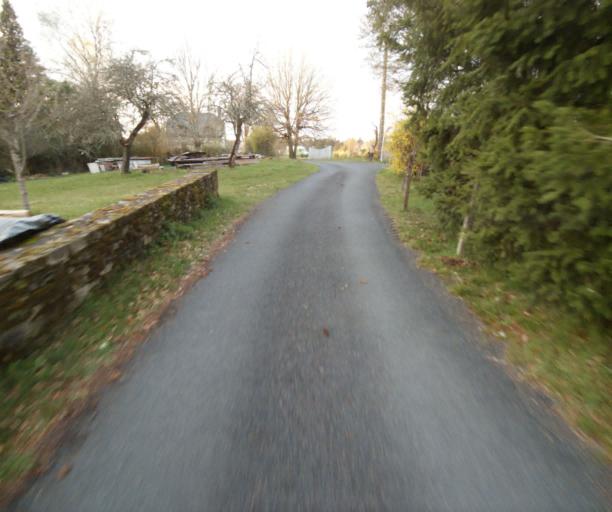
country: FR
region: Limousin
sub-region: Departement de la Correze
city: Argentat
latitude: 45.2448
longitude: 1.9828
